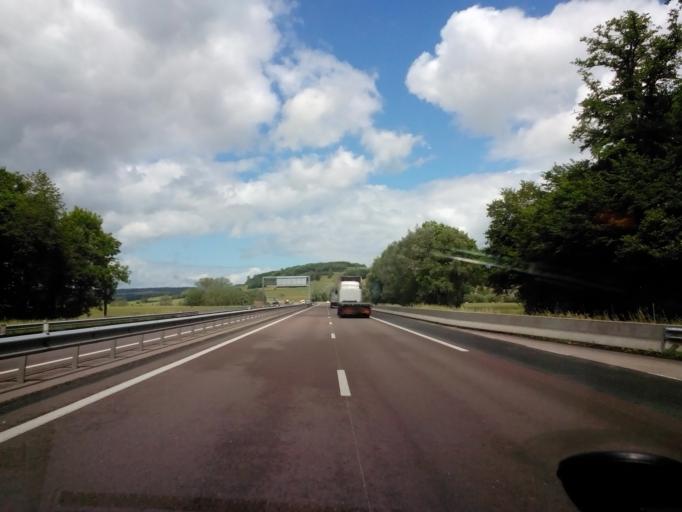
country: FR
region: Lorraine
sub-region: Departement des Vosges
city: Chatenois
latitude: 48.3216
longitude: 5.8555
